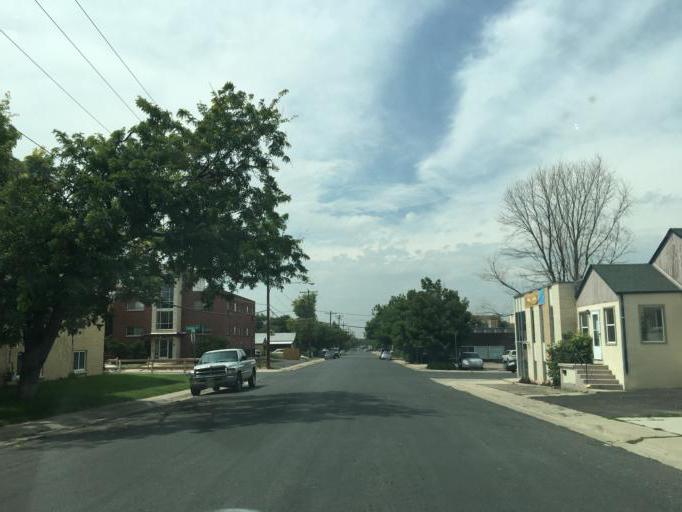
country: US
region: Colorado
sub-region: Adams County
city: Aurora
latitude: 39.7383
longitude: -104.8616
